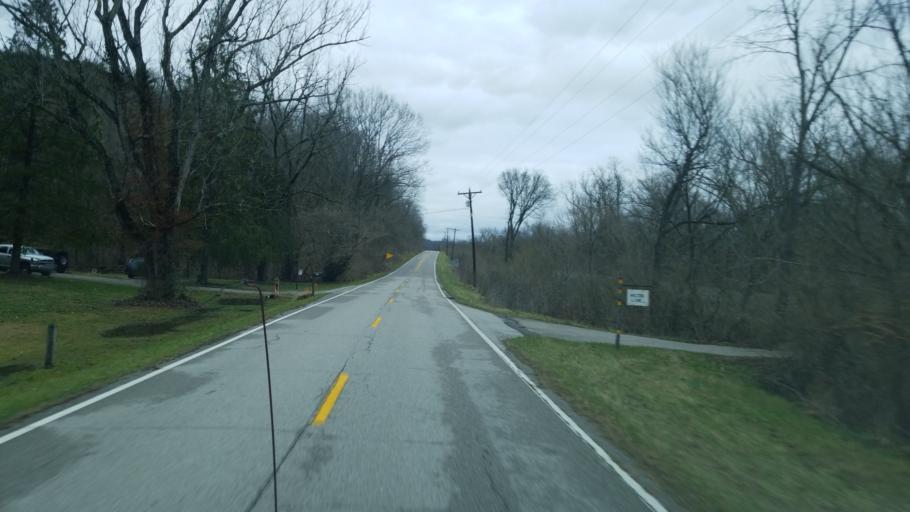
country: US
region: Ohio
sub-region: Clermont County
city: New Richmond
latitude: 38.9312
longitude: -84.2776
